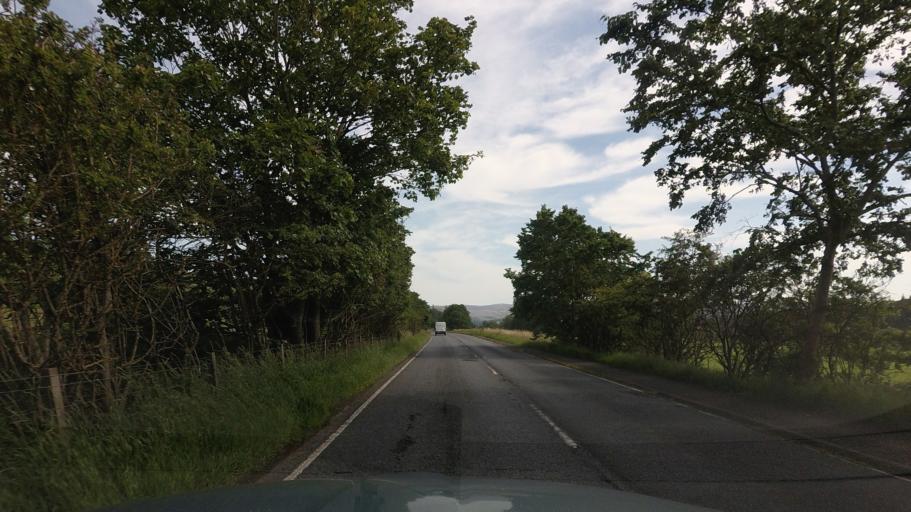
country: GB
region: Scotland
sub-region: The Scottish Borders
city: Peebles
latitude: 55.6718
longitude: -3.2005
